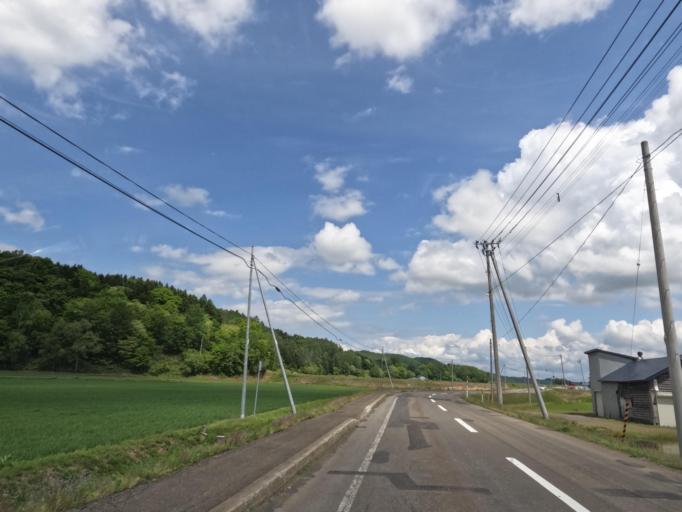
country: JP
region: Hokkaido
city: Takikawa
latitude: 43.5867
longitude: 141.7793
